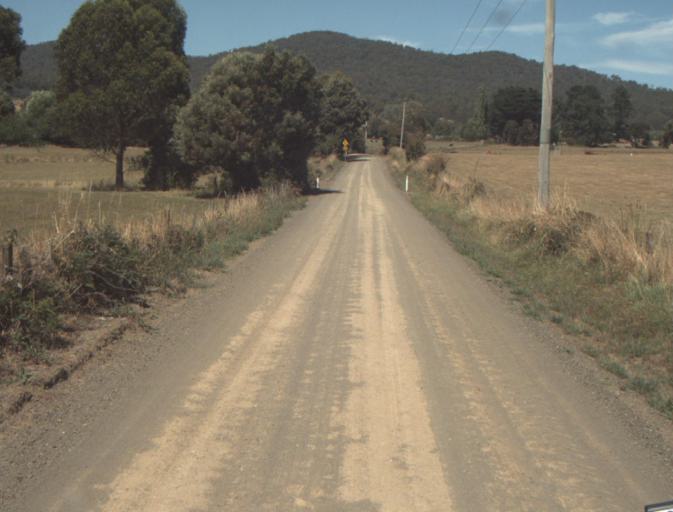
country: AU
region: Tasmania
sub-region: Launceston
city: Mayfield
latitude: -41.2569
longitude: 147.1331
